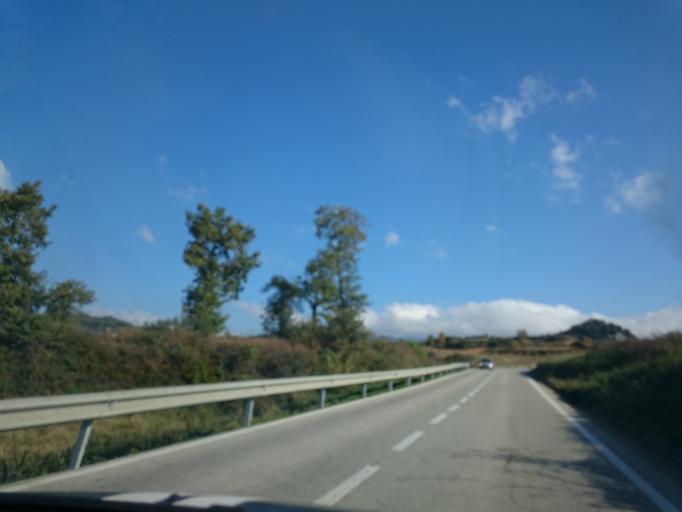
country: ES
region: Catalonia
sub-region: Provincia de Barcelona
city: Santa Maria de Corco
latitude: 42.0299
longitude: 2.3530
